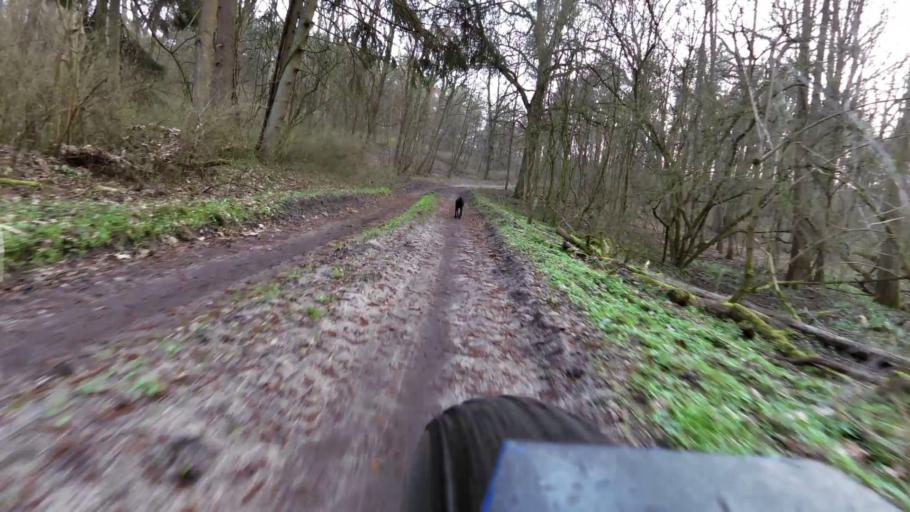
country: DE
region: Brandenburg
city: Vogelsang
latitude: 52.2794
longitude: 14.6967
